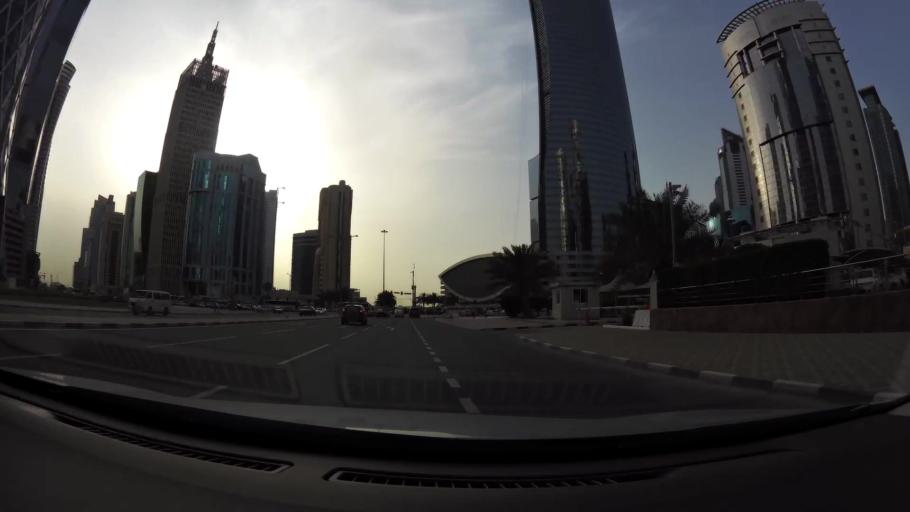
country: QA
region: Baladiyat ad Dawhah
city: Doha
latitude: 25.3203
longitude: 51.5286
